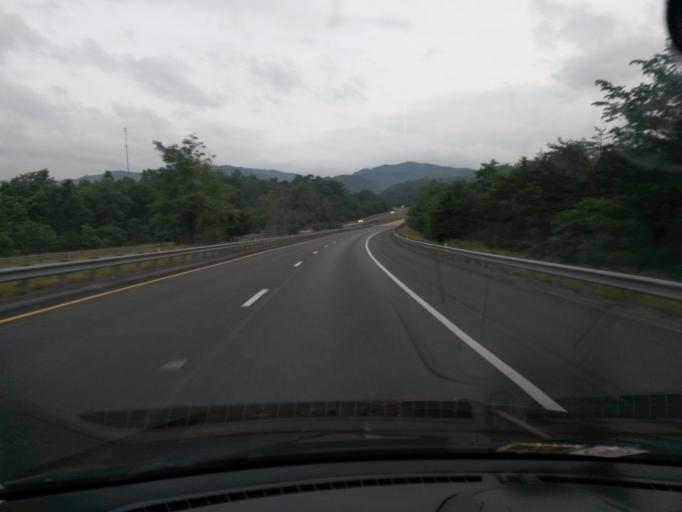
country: US
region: Virginia
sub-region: City of Covington
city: Covington
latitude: 37.8171
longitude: -80.1049
